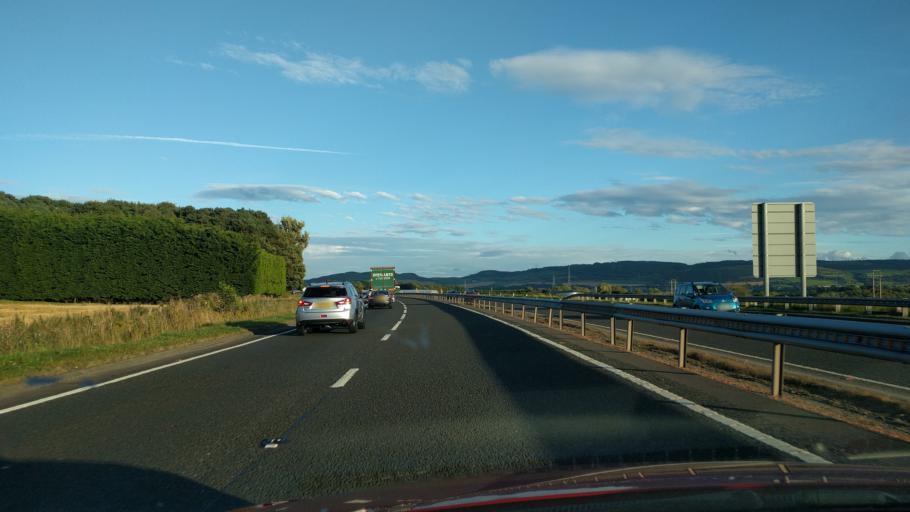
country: GB
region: Scotland
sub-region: Perth and Kinross
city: Abernethy
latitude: 56.3755
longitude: -3.3365
